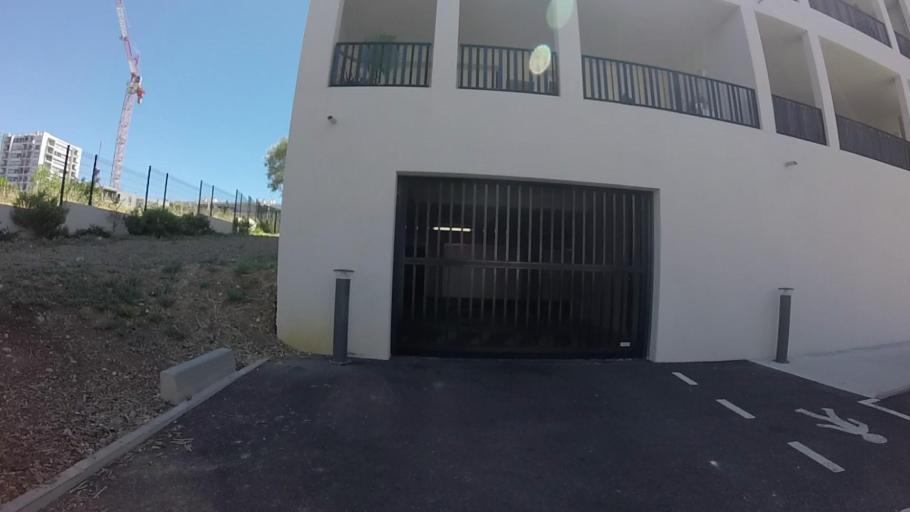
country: FR
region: Provence-Alpes-Cote d'Azur
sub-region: Departement des Alpes-Maritimes
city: Antibes
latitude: 43.5824
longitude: 7.1069
